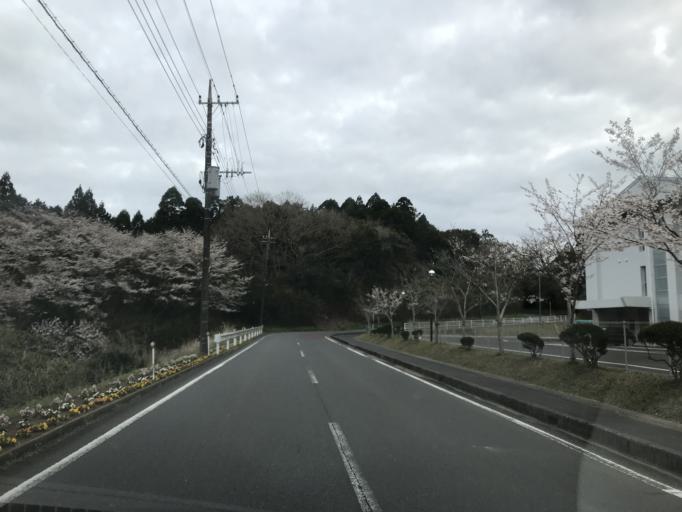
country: JP
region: Chiba
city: Omigawa
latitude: 35.8071
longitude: 140.5753
